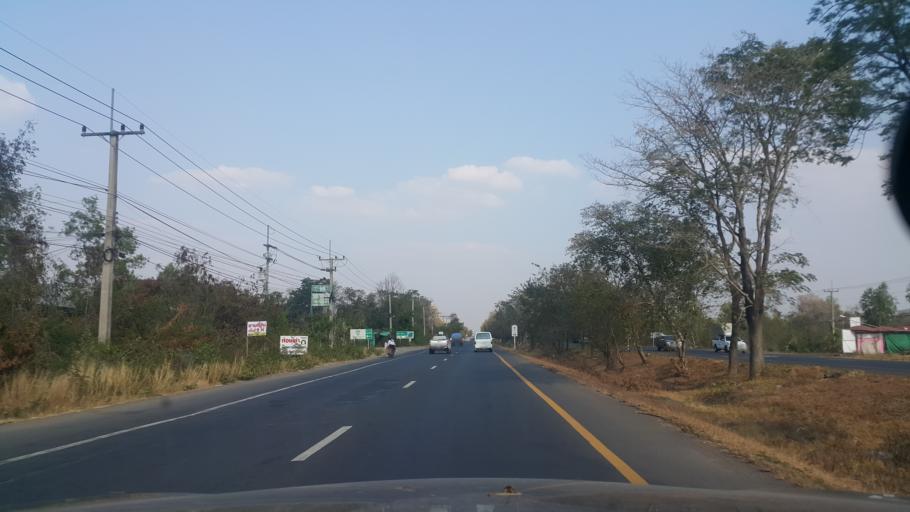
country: TH
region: Buriram
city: Nang Rong
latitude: 14.6331
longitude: 102.7245
